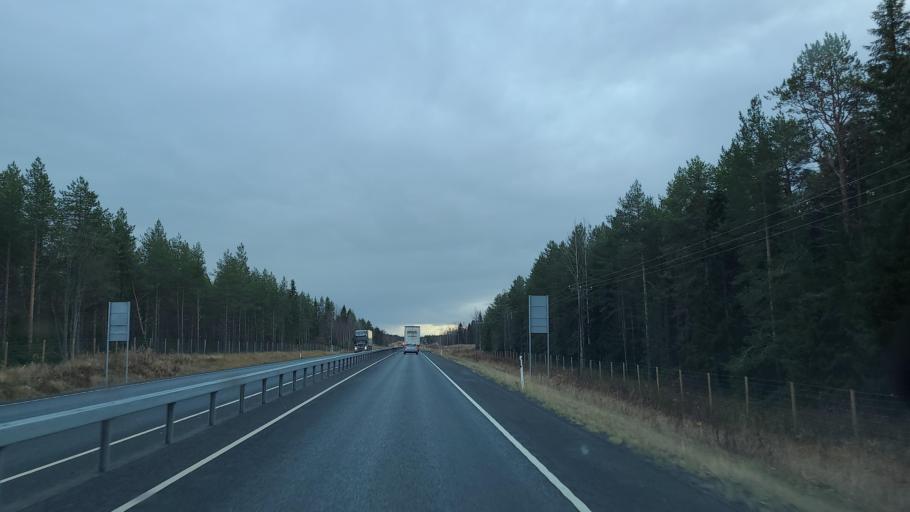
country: FI
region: Northern Ostrobothnia
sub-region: Oulunkaari
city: Kuivaniemi
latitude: 65.5560
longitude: 25.2384
